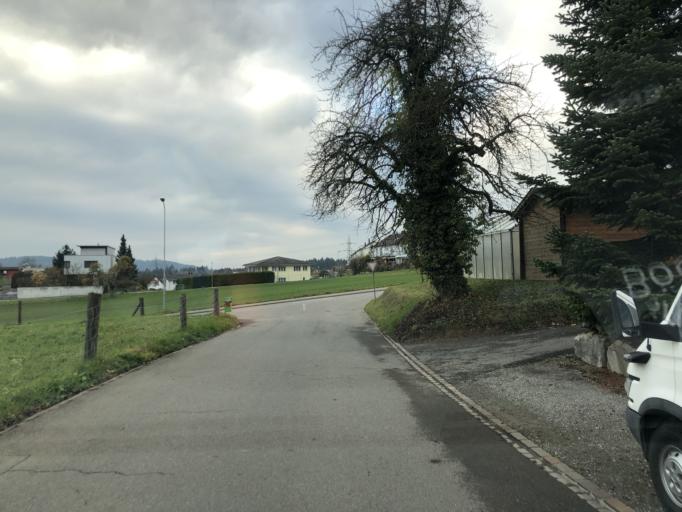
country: CH
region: Aargau
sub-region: Bezirk Baden
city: Niederrohrdorf
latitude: 47.4105
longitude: 8.3184
